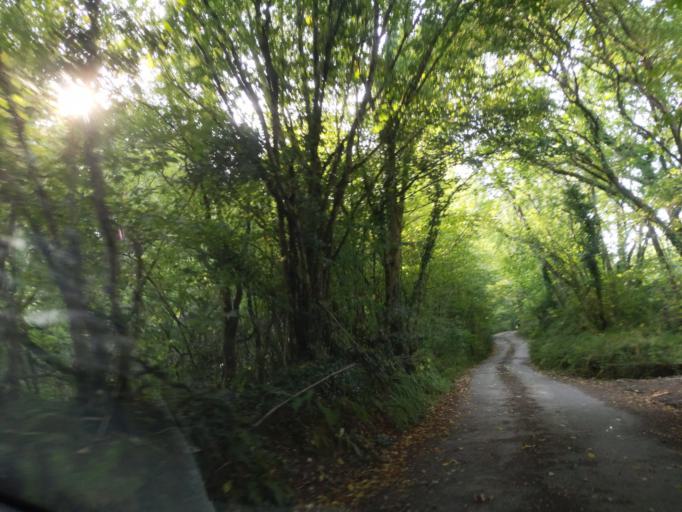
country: GB
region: England
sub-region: Devon
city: Winkleigh
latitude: 50.9670
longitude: -3.9674
